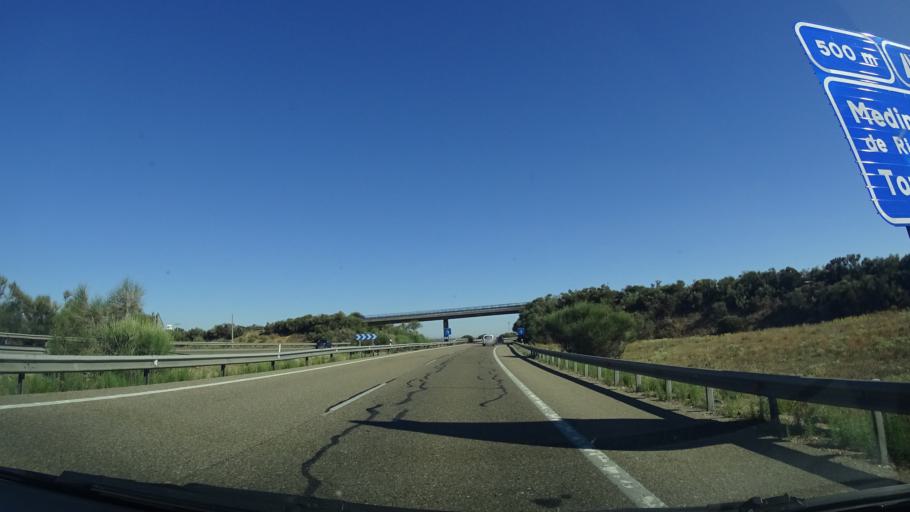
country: ES
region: Castille and Leon
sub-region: Provincia de Valladolid
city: Villardefrades
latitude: 41.7194
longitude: -5.2472
